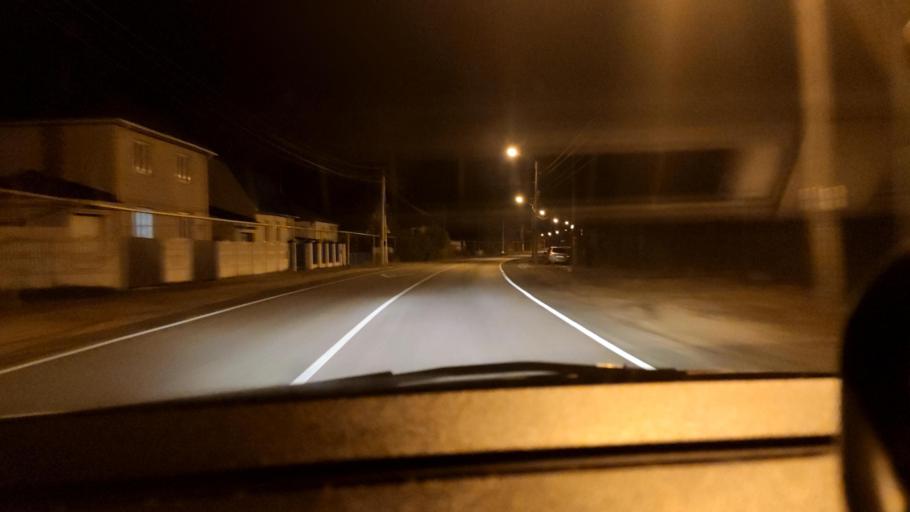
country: RU
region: Voronezj
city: Shilovo
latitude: 51.5528
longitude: 39.0759
